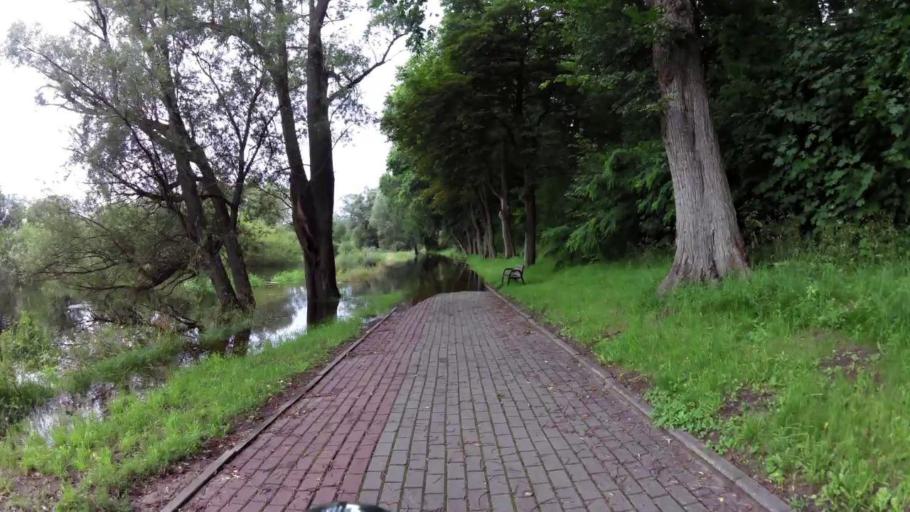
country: PL
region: West Pomeranian Voivodeship
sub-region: Powiat bialogardzki
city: Karlino
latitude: 54.0366
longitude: 15.8716
